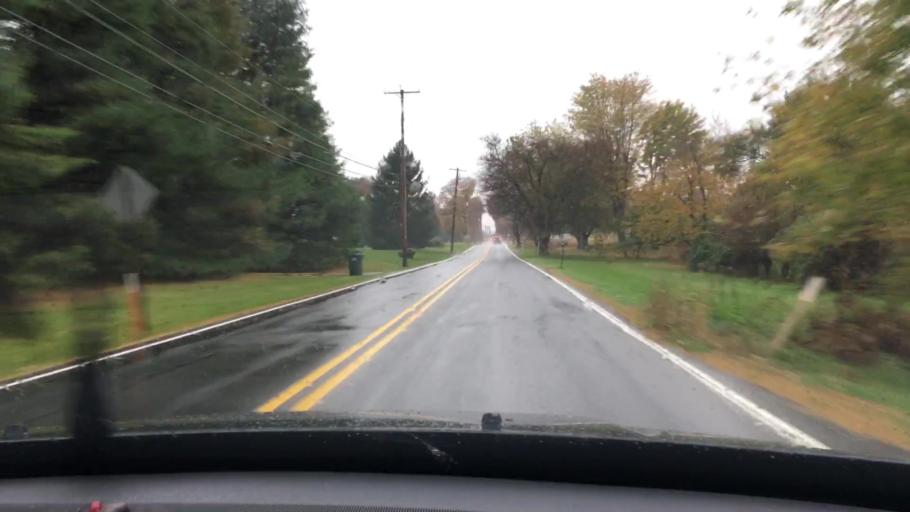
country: US
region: Pennsylvania
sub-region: York County
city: Stewartstown
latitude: 39.7243
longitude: -76.5280
